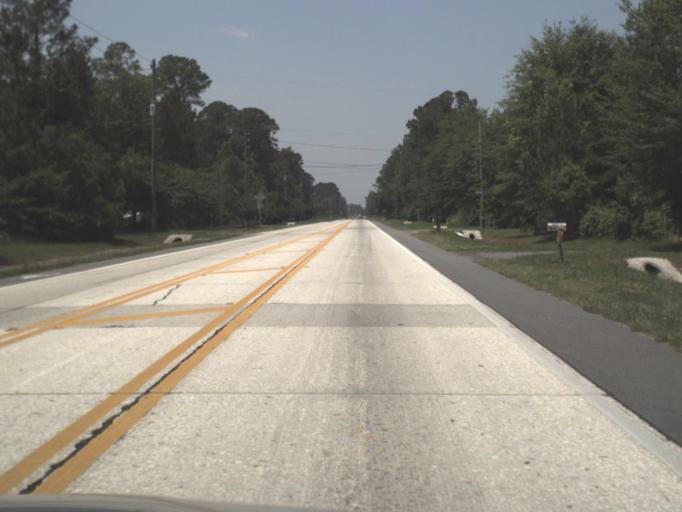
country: US
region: Florida
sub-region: Duval County
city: Baldwin
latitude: 30.2172
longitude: -81.9432
